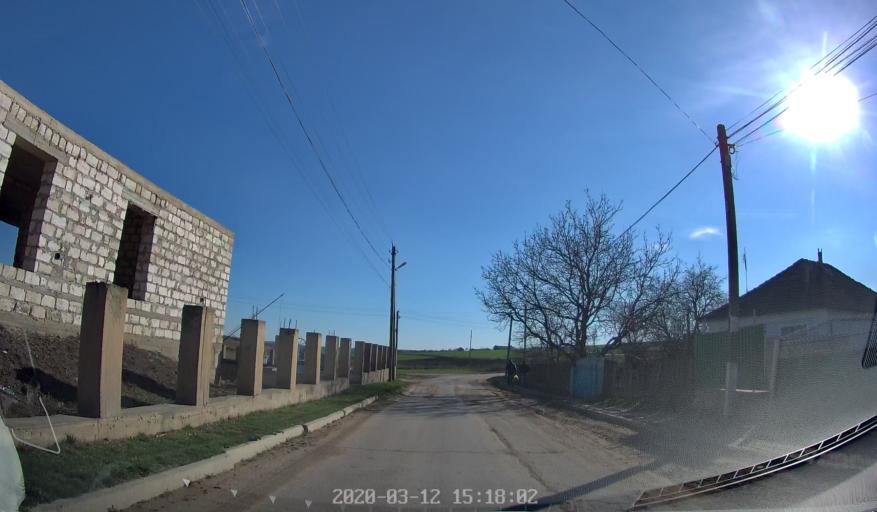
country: MD
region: Chisinau
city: Ciorescu
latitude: 47.2182
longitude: 28.9344
